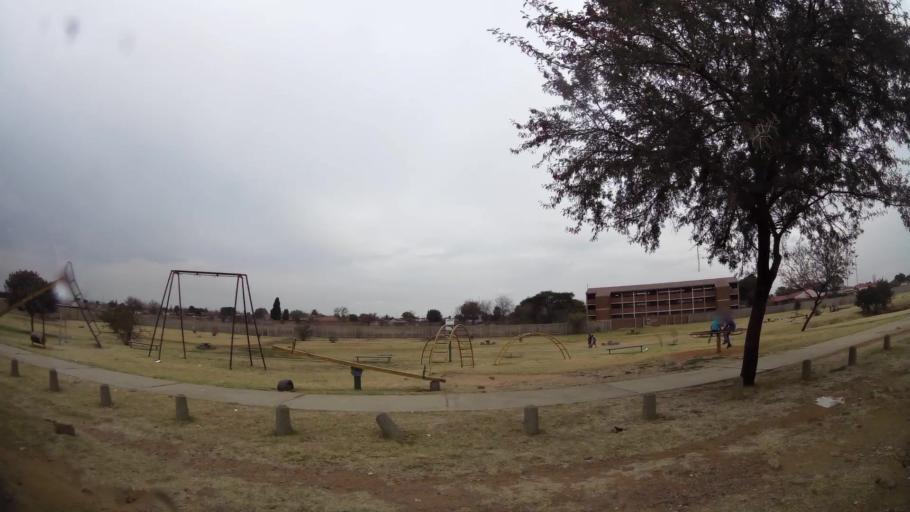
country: ZA
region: Gauteng
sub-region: City of Tshwane Metropolitan Municipality
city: Pretoria
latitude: -25.7058
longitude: 28.3524
